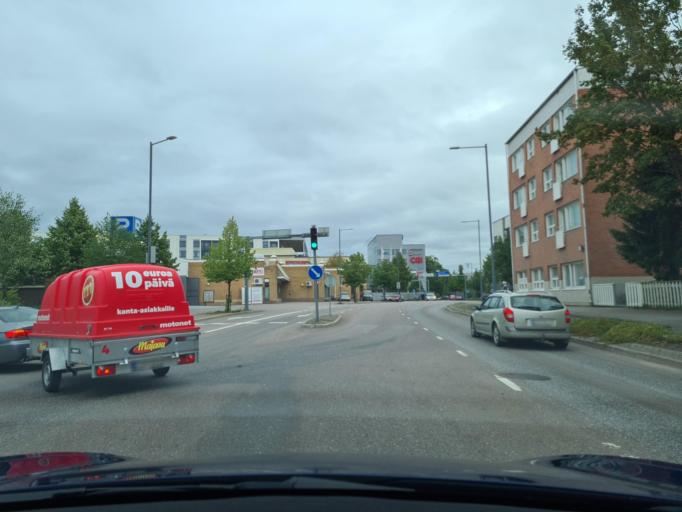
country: FI
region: South Karelia
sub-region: Lappeenranta
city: Lappeenranta
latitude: 61.0547
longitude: 28.1866
